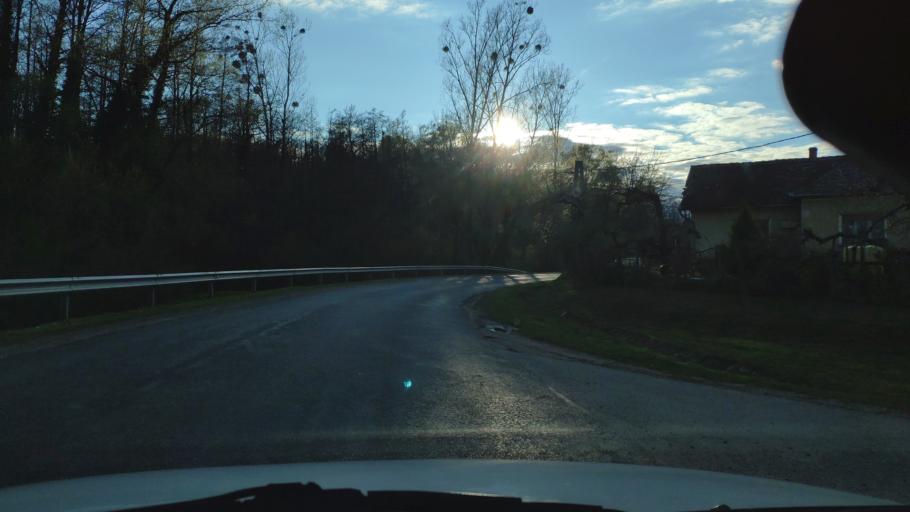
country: HU
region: Zala
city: Nagykanizsa
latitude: 46.4219
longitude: 17.1174
